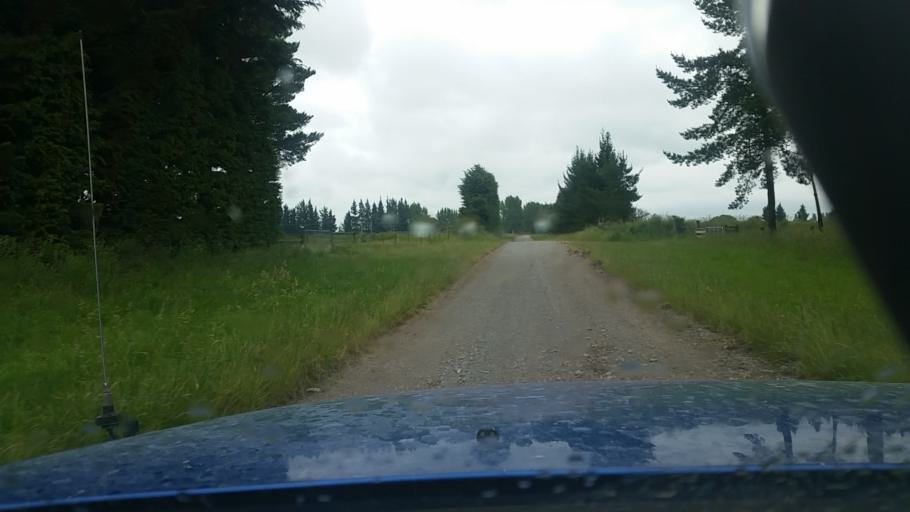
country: NZ
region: Canterbury
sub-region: Ashburton District
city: Ashburton
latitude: -43.7845
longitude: 171.6345
